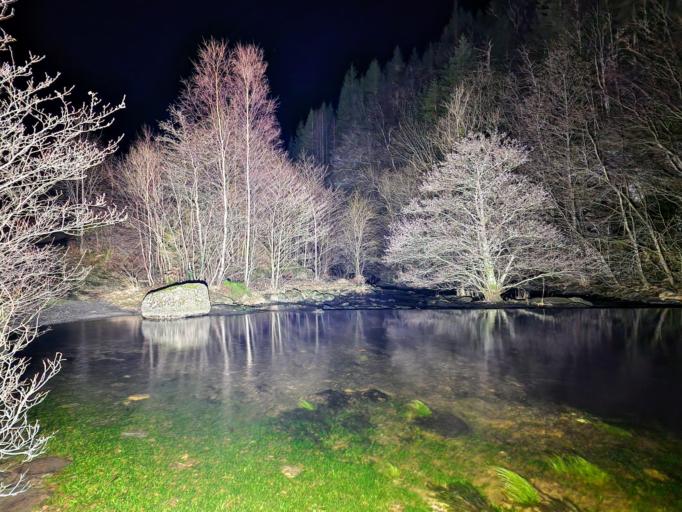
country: NO
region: Rogaland
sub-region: Finnoy
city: Judaberg
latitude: 59.3506
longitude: 5.8032
